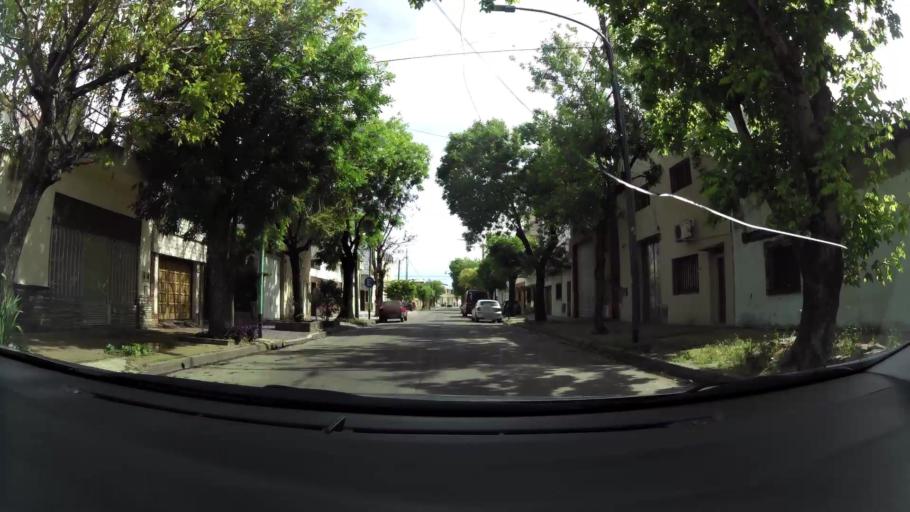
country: AR
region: Buenos Aires F.D.
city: Villa Lugano
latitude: -34.6573
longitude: -58.4274
